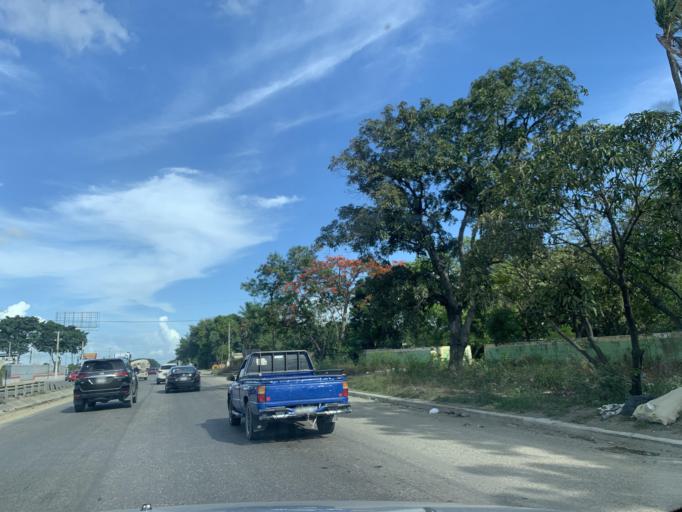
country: DO
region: Santiago
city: Villa Gonzalez
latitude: 19.5431
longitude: -70.8009
